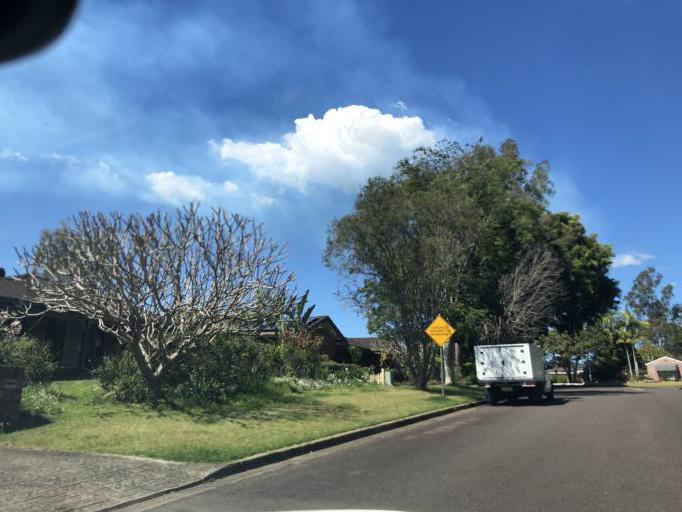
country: AU
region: New South Wales
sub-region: Bellingen
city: Bellingen
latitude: -30.4583
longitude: 152.9033
